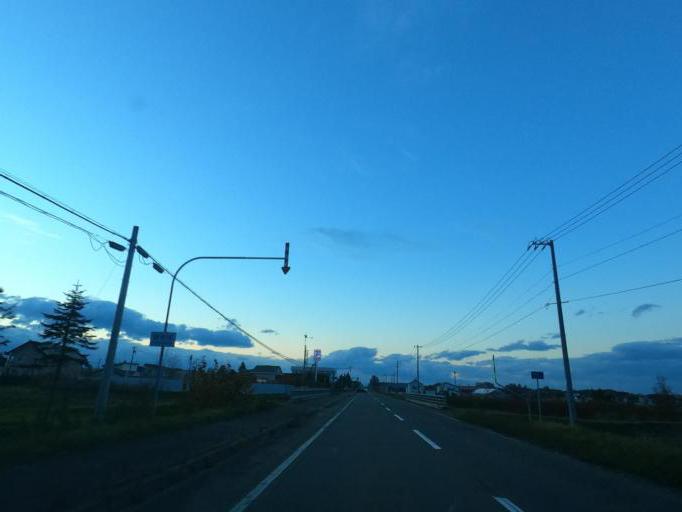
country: JP
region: Hokkaido
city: Obihiro
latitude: 42.6485
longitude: 143.1951
